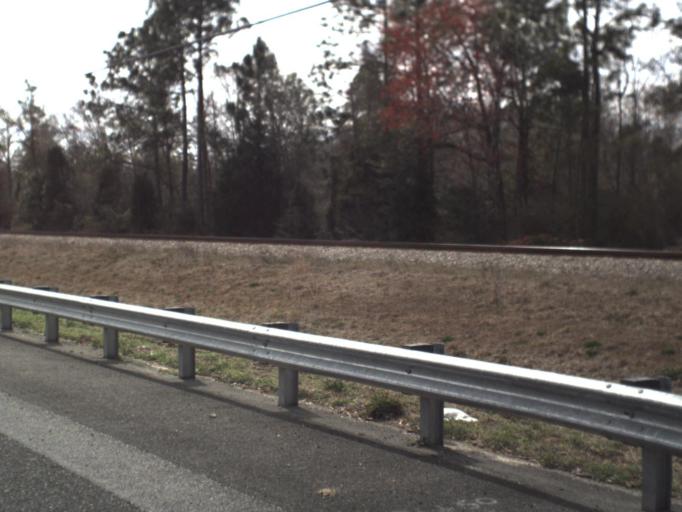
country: US
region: Florida
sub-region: Washington County
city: Chipley
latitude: 30.7135
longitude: -85.3908
